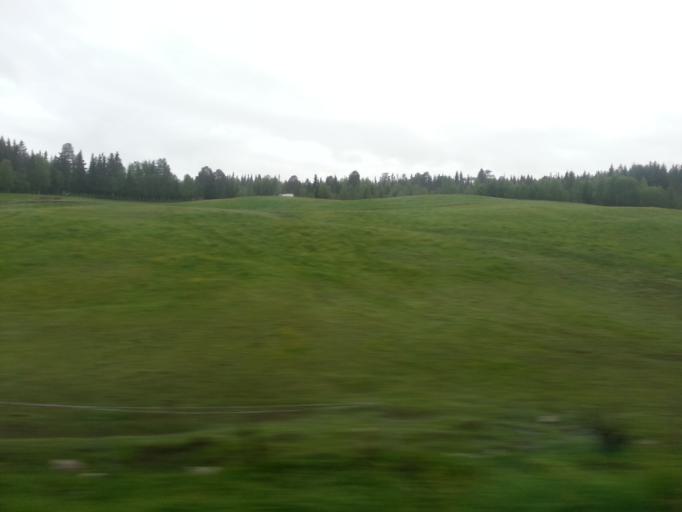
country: NO
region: Sor-Trondelag
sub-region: Rennebu
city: Berkak
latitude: 62.8689
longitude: 10.0480
